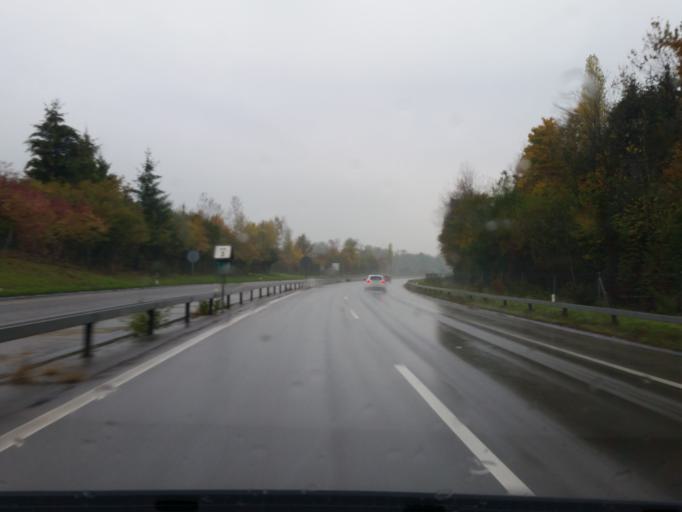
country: CH
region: Thurgau
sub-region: Weinfelden District
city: Wigoltingen
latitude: 47.5814
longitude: 9.0247
